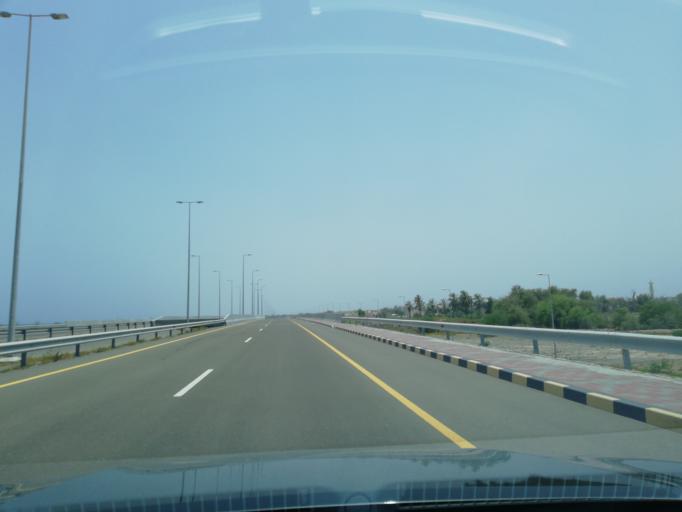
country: OM
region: Al Batinah
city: Shinas
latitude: 24.7686
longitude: 56.4598
